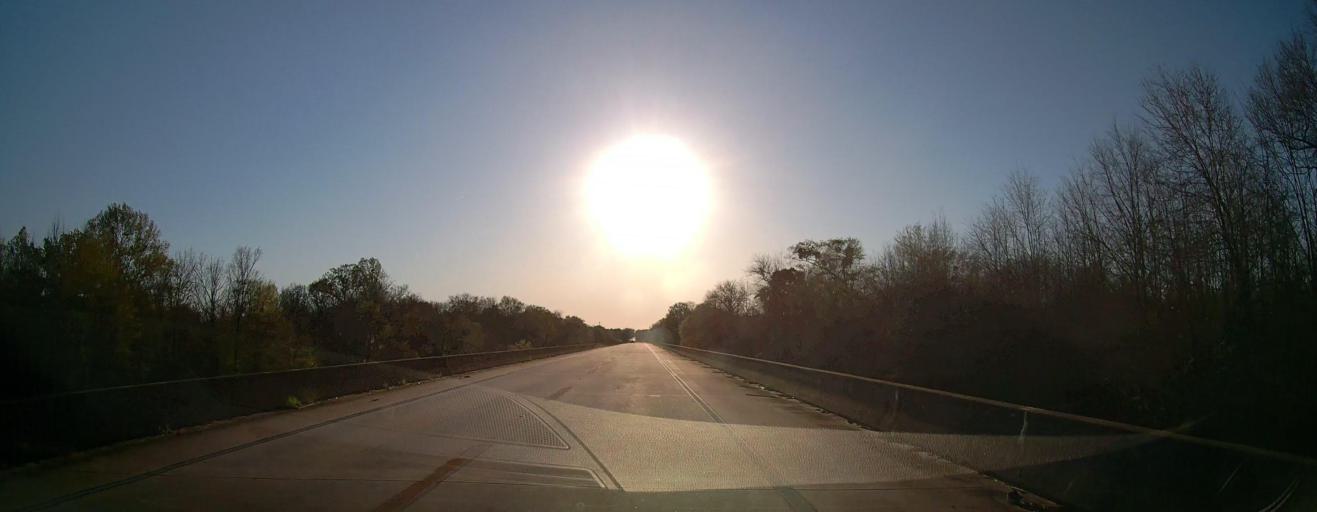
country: US
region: Georgia
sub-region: Wilcox County
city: Abbeville
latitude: 31.9970
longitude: -83.2776
